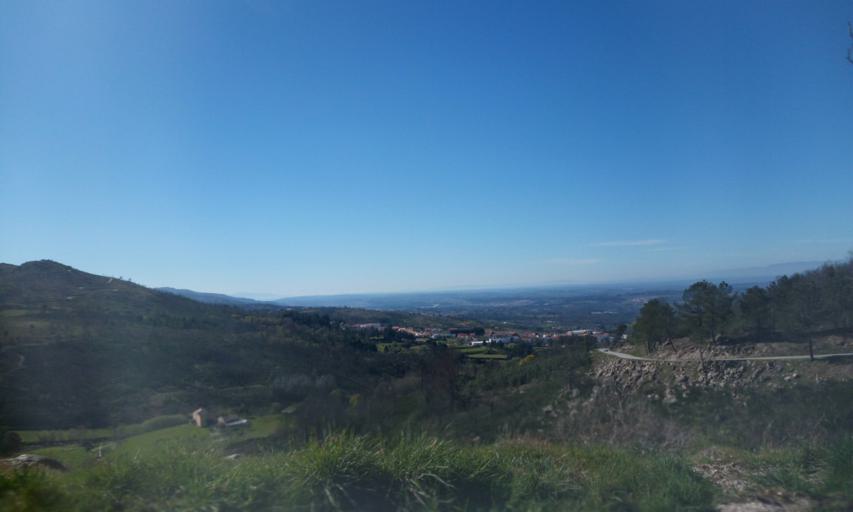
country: PT
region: Guarda
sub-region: Manteigas
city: Manteigas
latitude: 40.4913
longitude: -7.5762
